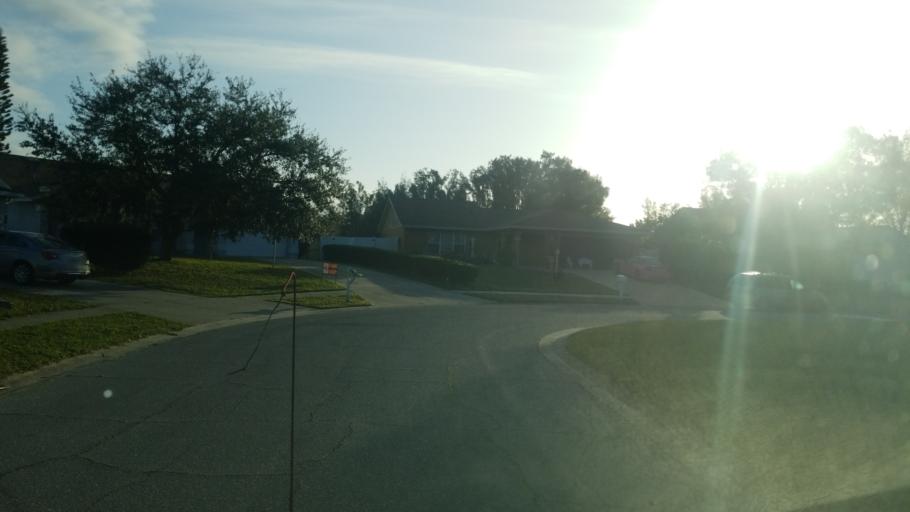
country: US
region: Florida
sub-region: Manatee County
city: Samoset
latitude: 27.4425
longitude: -82.5317
